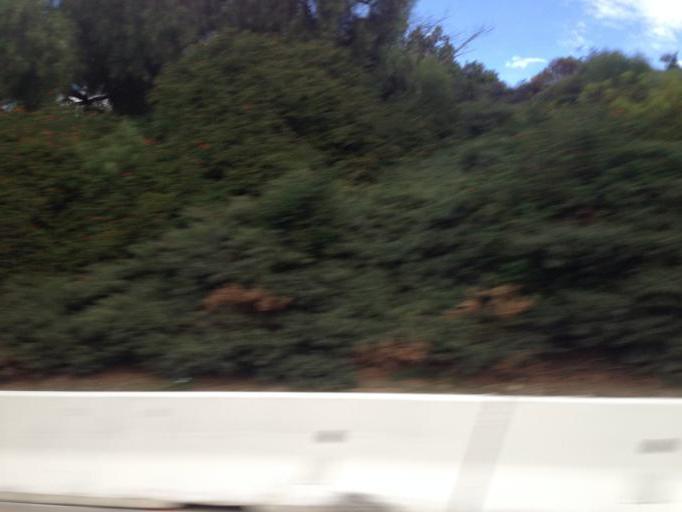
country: US
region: California
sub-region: San Diego County
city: National City
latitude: 32.6726
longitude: -117.0823
